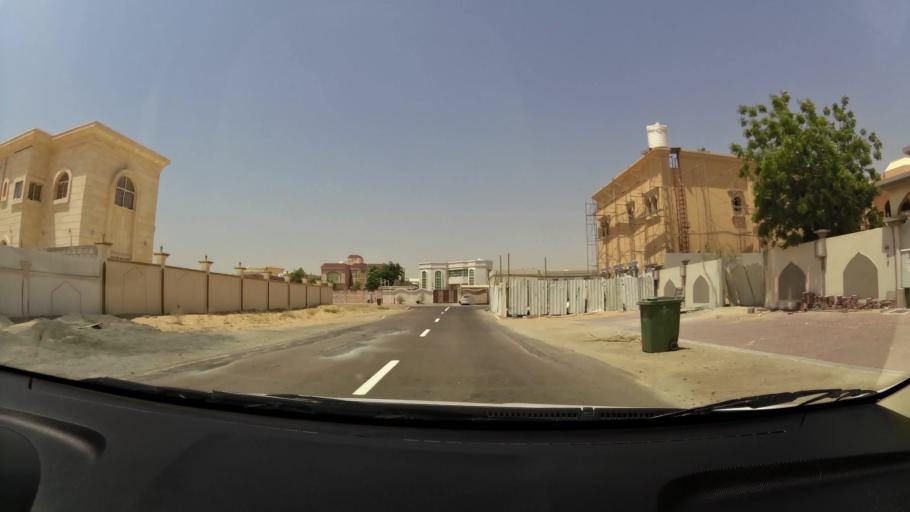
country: AE
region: Ajman
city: Ajman
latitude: 25.4230
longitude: 55.5151
